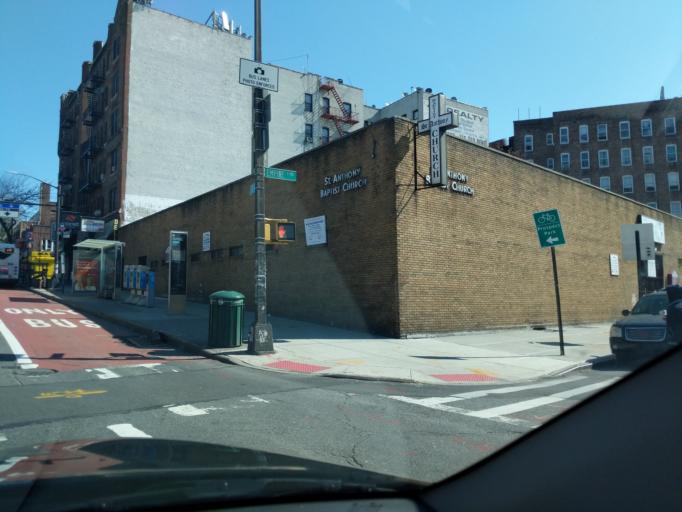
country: US
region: New York
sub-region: Kings County
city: Brooklyn
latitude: 40.6622
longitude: -73.9311
